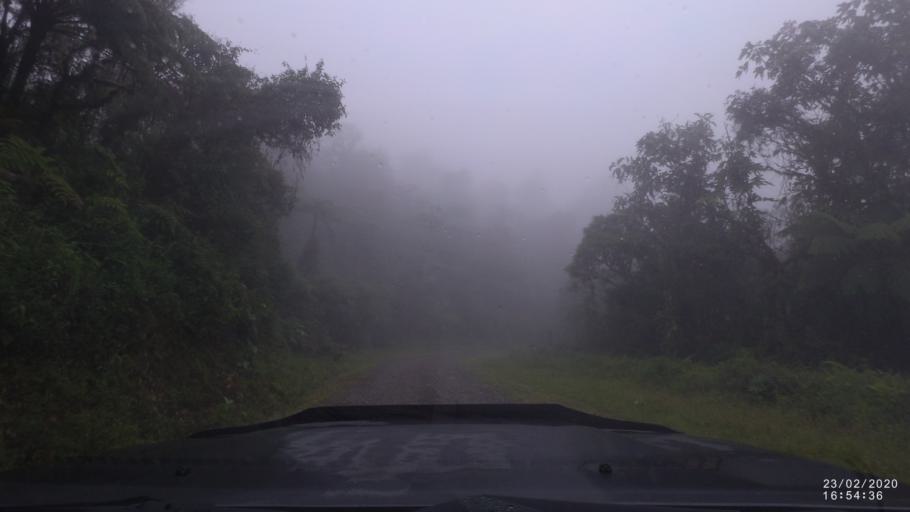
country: BO
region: Cochabamba
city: Colomi
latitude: -17.0999
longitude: -65.9819
